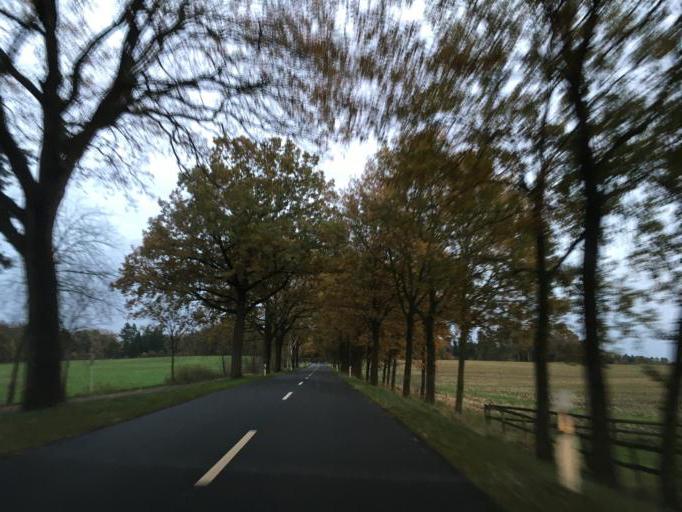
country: DE
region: Lower Saxony
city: Bispingen
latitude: 53.0999
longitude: 10.0069
